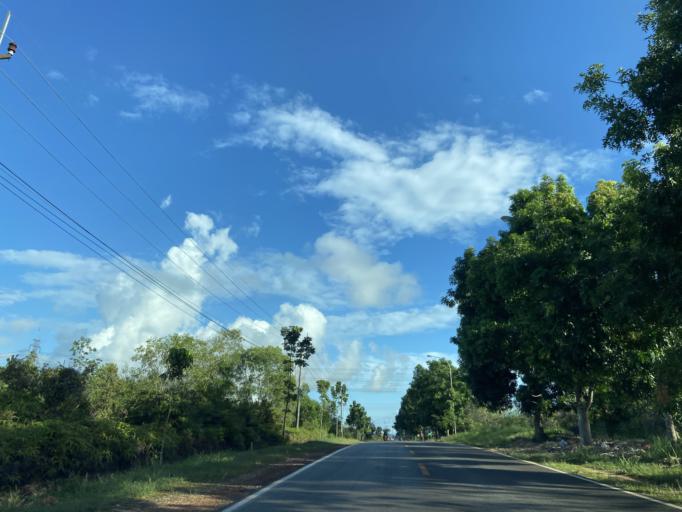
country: SG
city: Singapore
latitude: 1.0167
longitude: 104.0169
